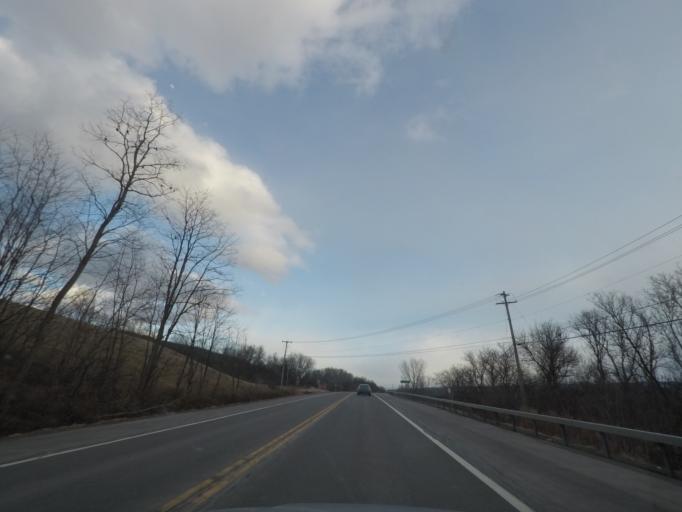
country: US
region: New York
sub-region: Herkimer County
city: Frankfort
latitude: 43.0455
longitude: -75.0624
